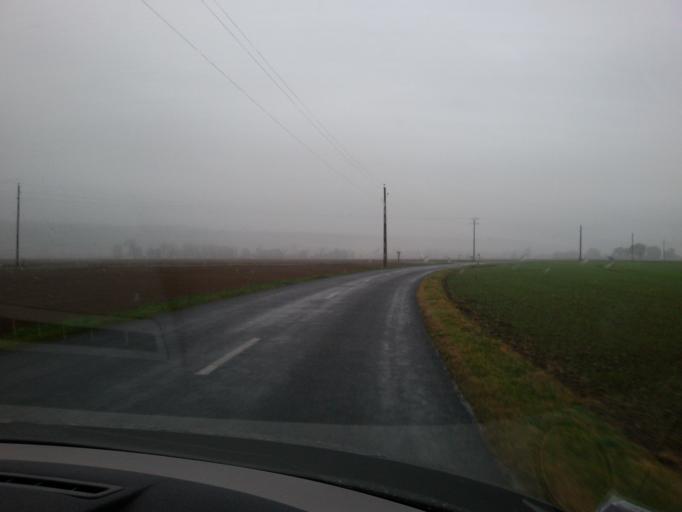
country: FR
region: Haute-Normandie
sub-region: Departement de l'Eure
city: Beuzeville
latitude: 49.4231
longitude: 0.3820
